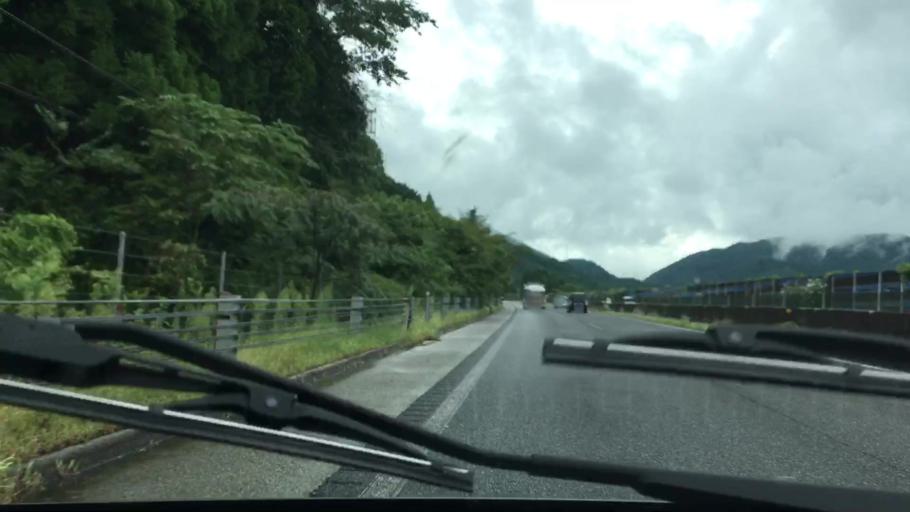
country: JP
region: Hyogo
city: Yamazakicho-nakabirose
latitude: 35.0194
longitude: 134.5025
